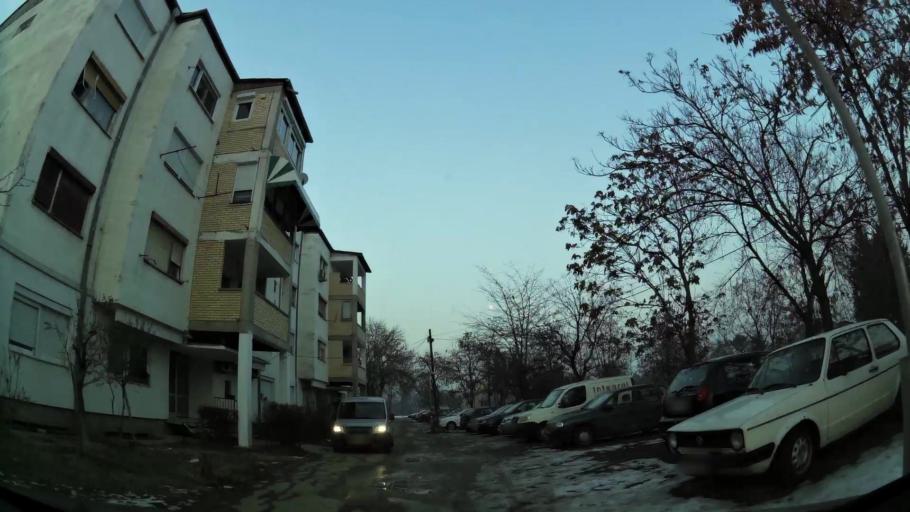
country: MK
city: Creshevo
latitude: 42.0056
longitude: 21.5064
